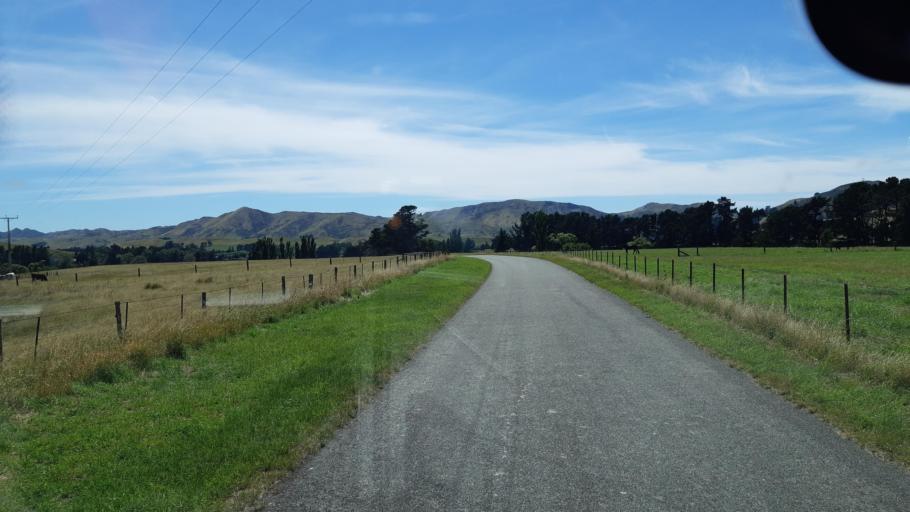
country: NZ
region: Marlborough
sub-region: Marlborough District
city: Blenheim
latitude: -41.8288
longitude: 174.1141
